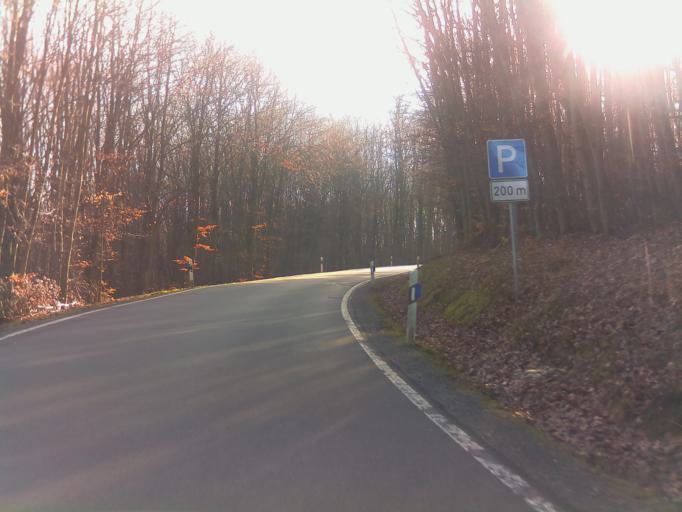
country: DE
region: Bavaria
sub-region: Regierungsbezirk Unterfranken
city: Monchberg
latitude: 49.7960
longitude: 9.2932
